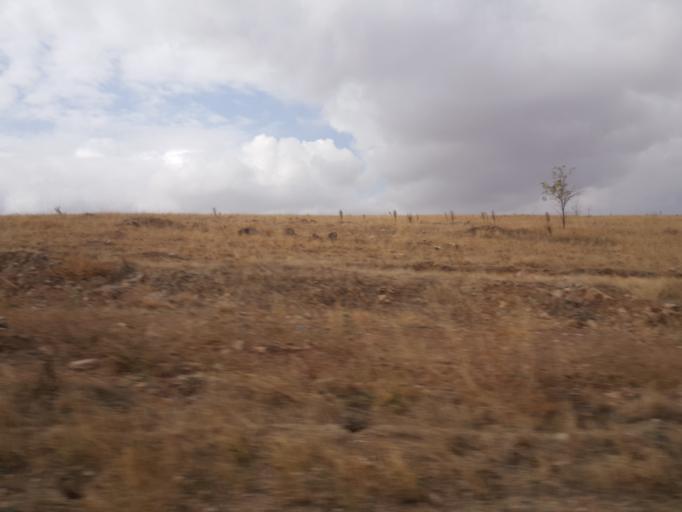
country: TR
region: Kirikkale
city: Keskin
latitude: 39.6494
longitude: 33.6194
